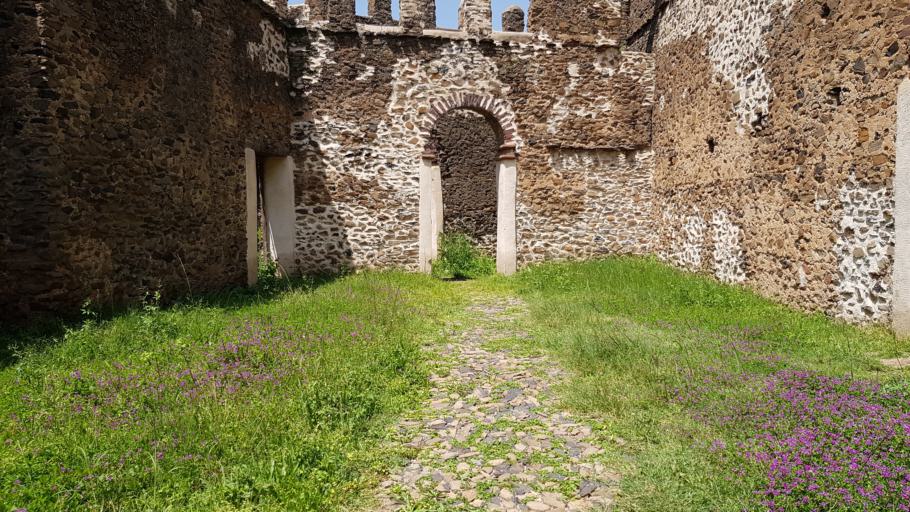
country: ET
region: Amhara
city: Gondar
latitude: 12.6092
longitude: 37.4697
